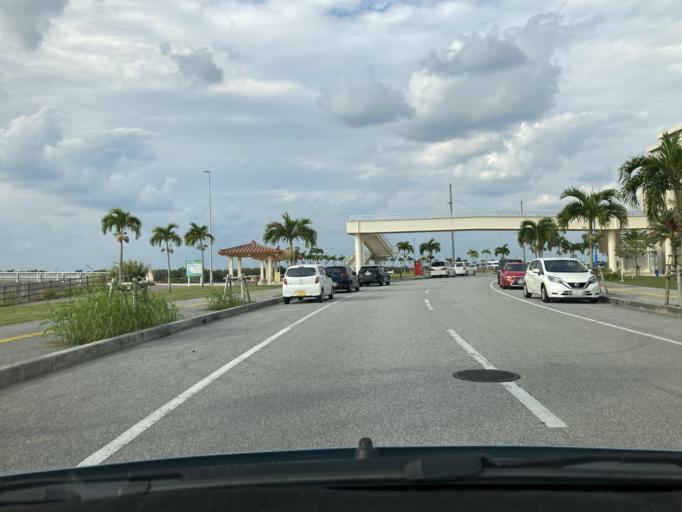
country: JP
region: Okinawa
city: Itoman
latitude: 26.1571
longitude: 127.6497
